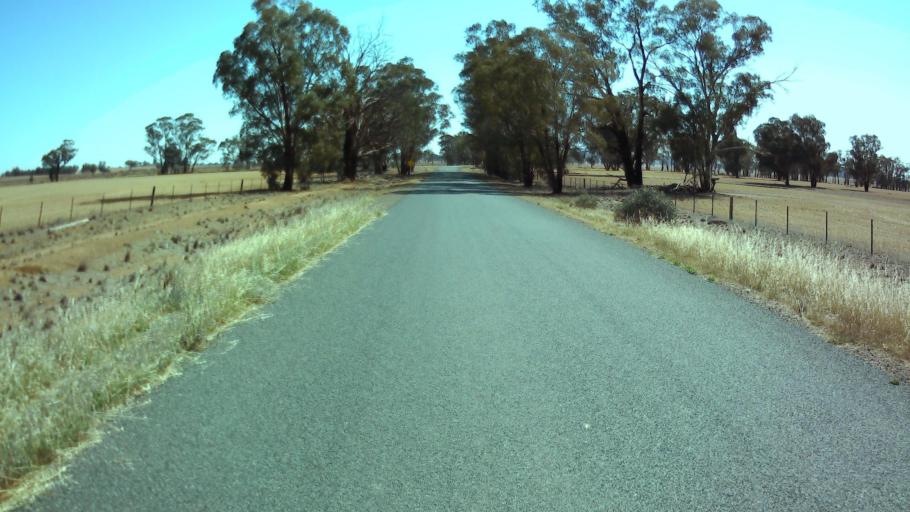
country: AU
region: New South Wales
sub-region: Weddin
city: Grenfell
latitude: -33.7313
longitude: 147.8885
